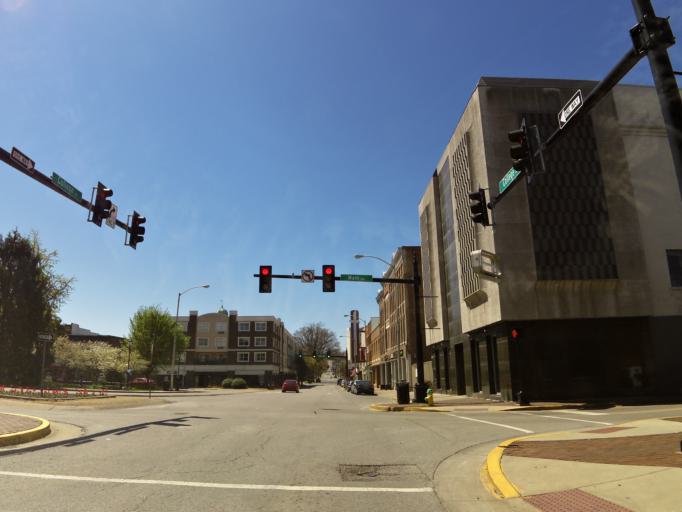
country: US
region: Kentucky
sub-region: Warren County
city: Bowling Green
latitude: 36.9939
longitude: -86.4415
